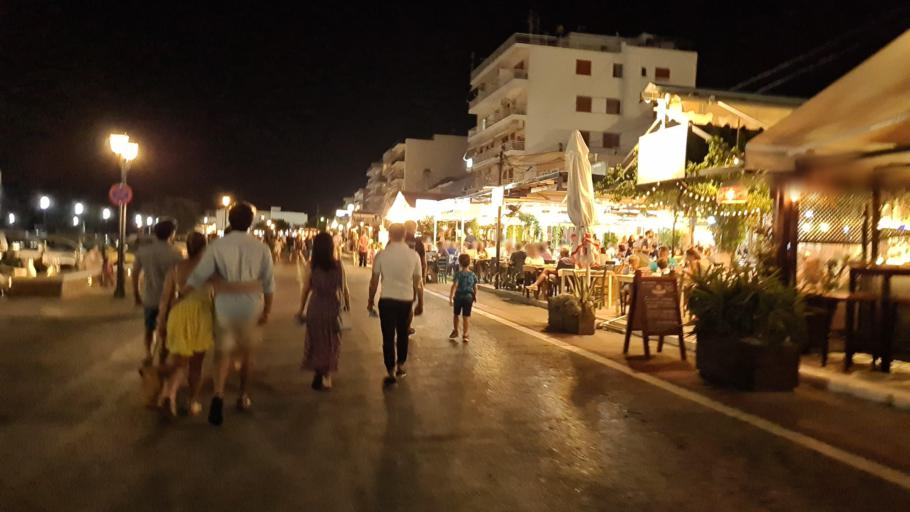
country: GR
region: Central Greece
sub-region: Nomos Evvoias
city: Karystos
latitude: 38.0133
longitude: 24.4183
